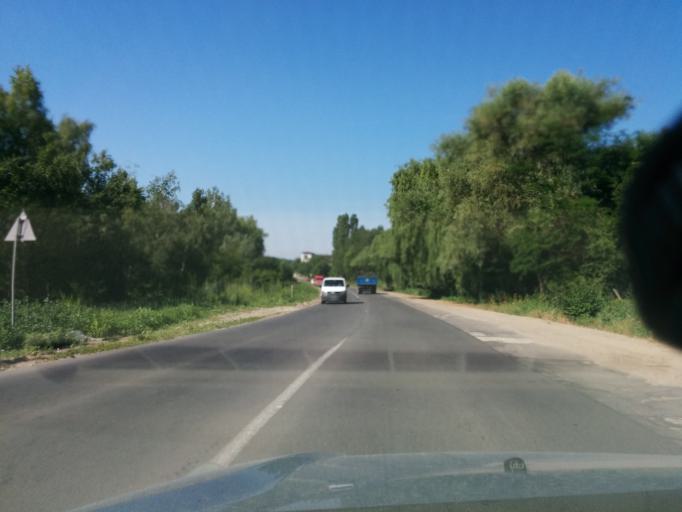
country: MD
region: Chisinau
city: Stauceni
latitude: 47.0555
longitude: 28.9408
